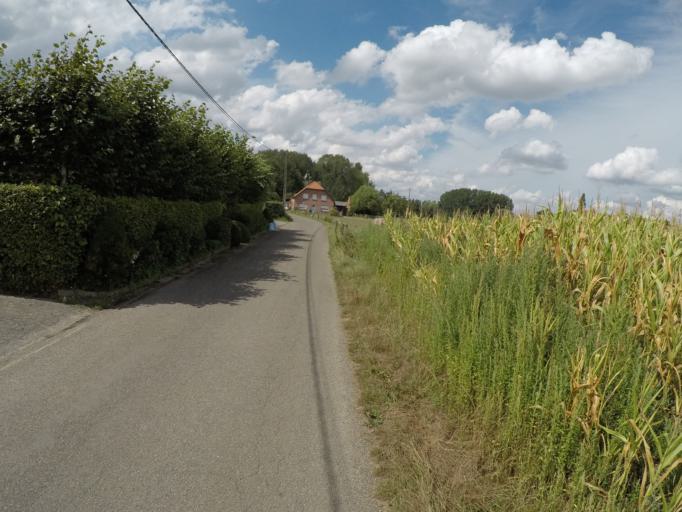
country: BE
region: Flanders
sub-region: Provincie Antwerpen
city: Ranst
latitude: 51.1848
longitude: 4.5406
